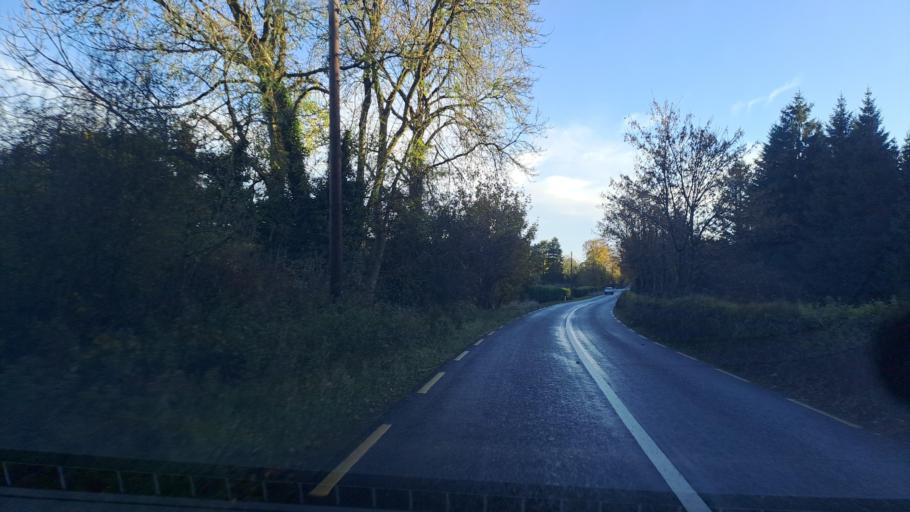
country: IE
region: Ulster
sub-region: An Cabhan
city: Cootehill
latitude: 54.1102
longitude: -7.0508
